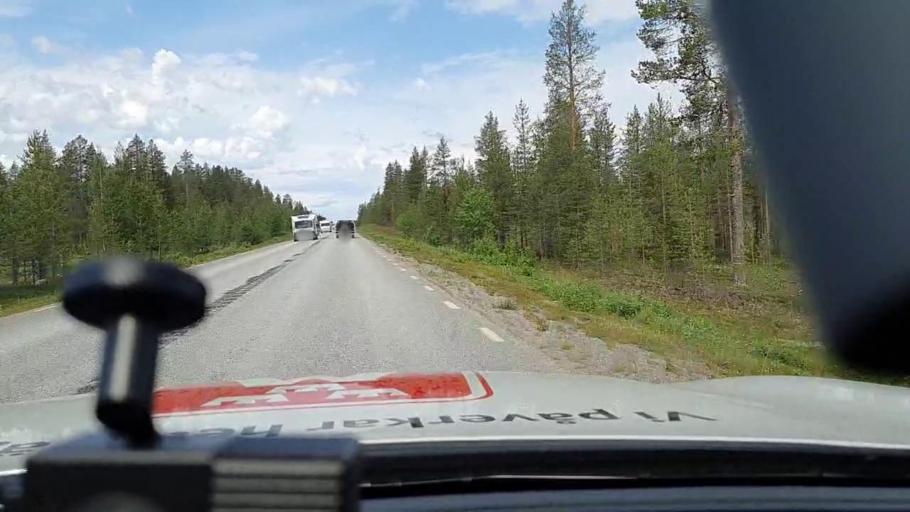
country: SE
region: Norrbotten
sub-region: Jokkmokks Kommun
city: Jokkmokk
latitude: 66.5219
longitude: 20.2099
